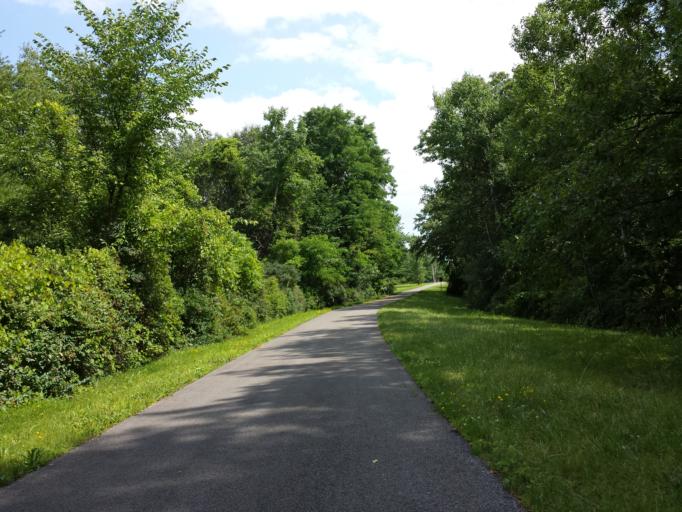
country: US
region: New York
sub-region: Saratoga County
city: Ballston Spa
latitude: 42.9690
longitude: -73.8280
